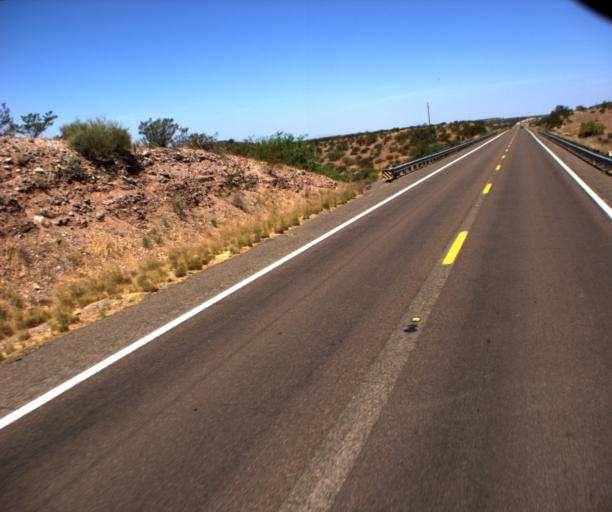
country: US
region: Arizona
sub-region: Graham County
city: Bylas
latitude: 33.2027
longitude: -110.1922
